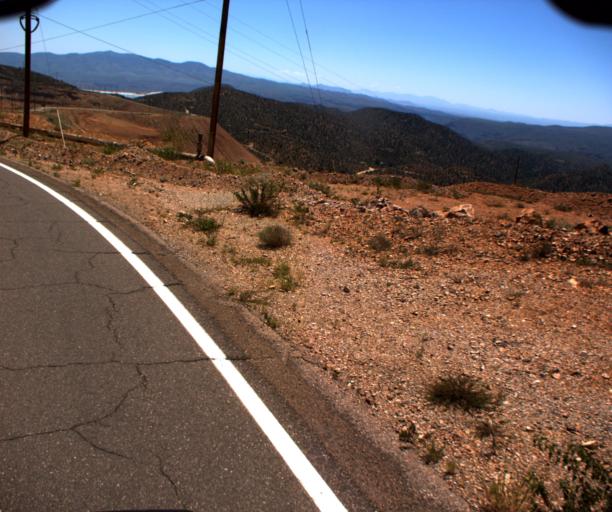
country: US
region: Arizona
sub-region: Greenlee County
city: Morenci
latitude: 33.0875
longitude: -109.3829
